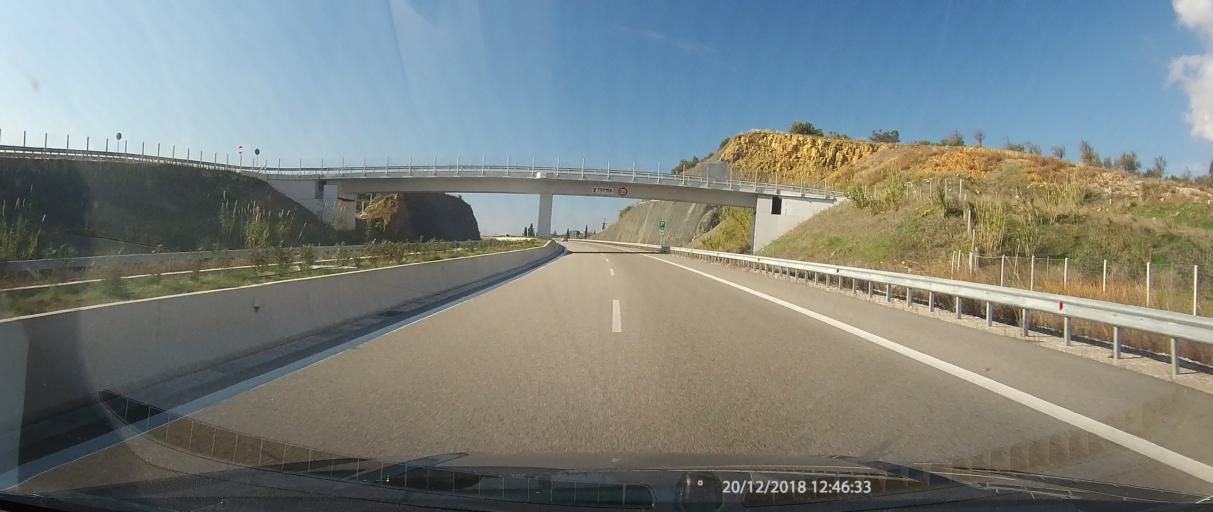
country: GR
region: West Greece
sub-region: Nomos Aitolias kai Akarnanias
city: Mesolongi
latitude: 38.3930
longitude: 21.4709
